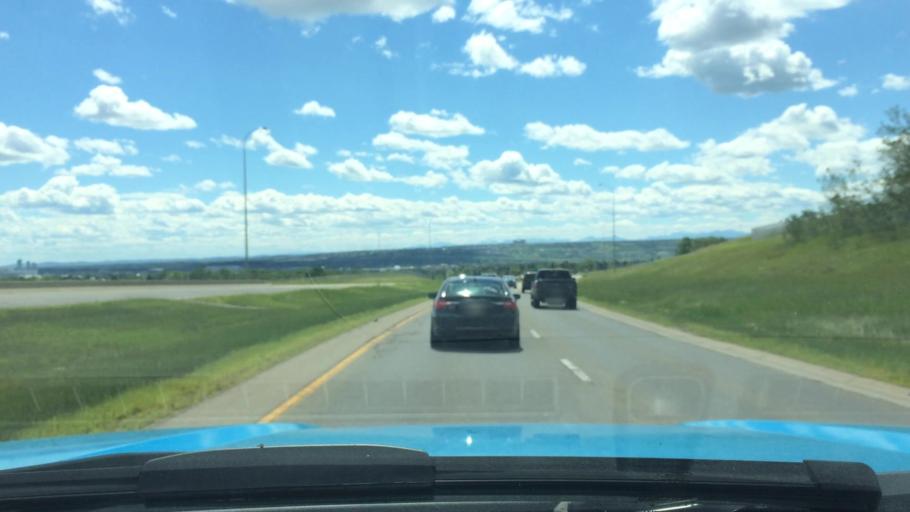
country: CA
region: Alberta
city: Calgary
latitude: 51.1146
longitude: -114.1349
